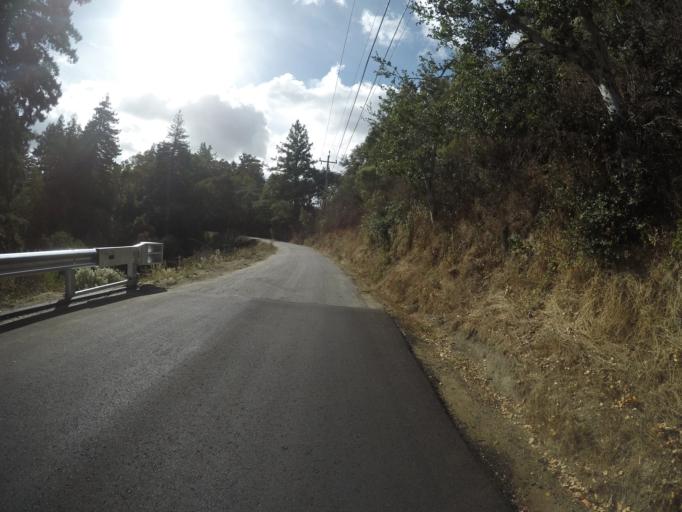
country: US
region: California
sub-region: Santa Cruz County
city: Scotts Valley
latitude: 37.0450
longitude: -121.9653
